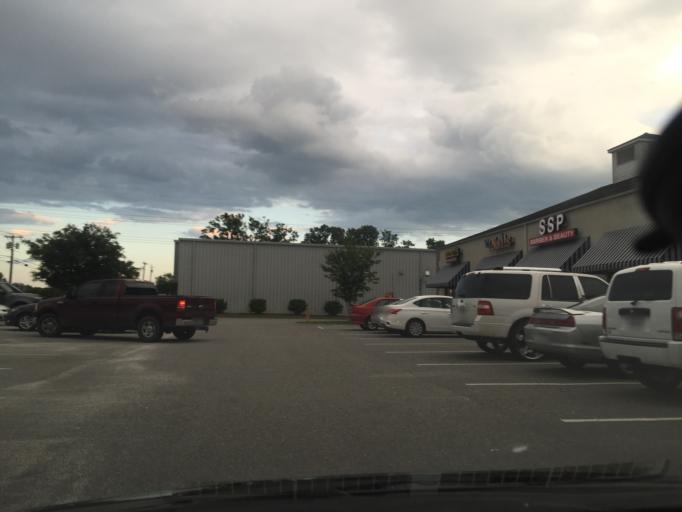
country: US
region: Georgia
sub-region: Chatham County
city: Pooler
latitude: 32.1060
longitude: -81.2286
